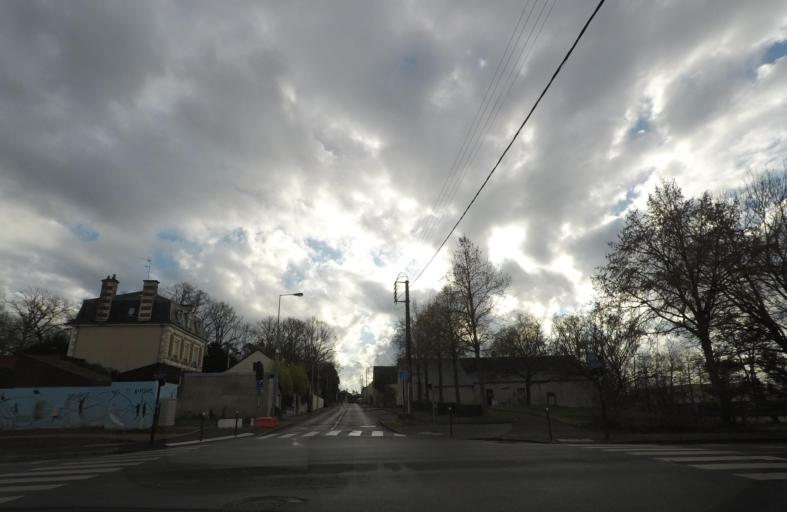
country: FR
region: Centre
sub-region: Departement du Cher
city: Bourges
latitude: 47.0633
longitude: 2.4001
